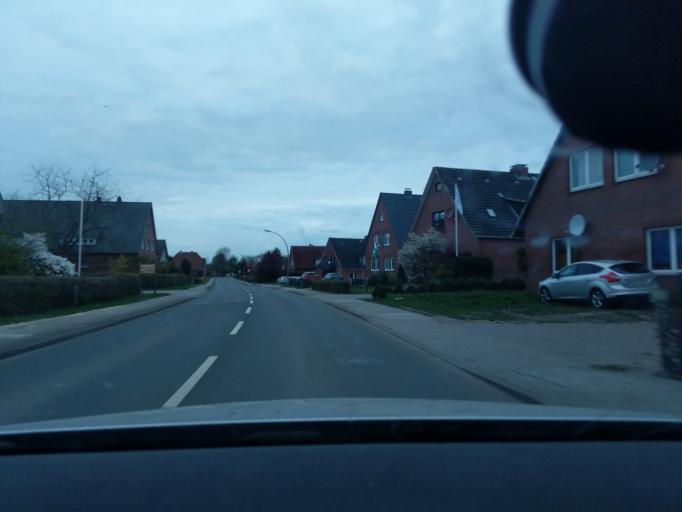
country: DE
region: Lower Saxony
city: Neu Wulmstorf
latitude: 53.5142
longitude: 9.8010
